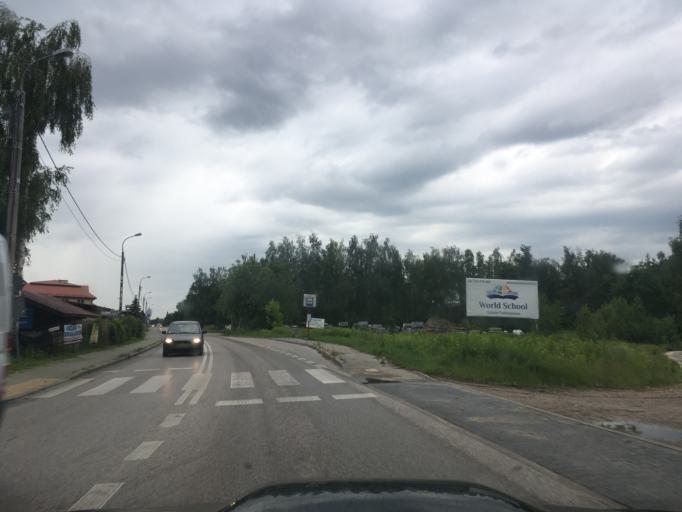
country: PL
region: Masovian Voivodeship
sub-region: Powiat piaseczynski
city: Zalesie Gorne
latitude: 52.0390
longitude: 21.0137
